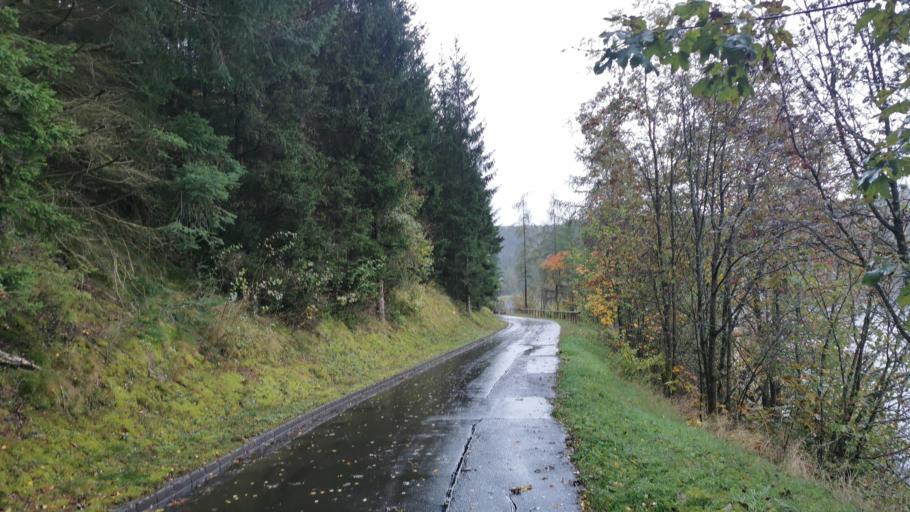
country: DE
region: Bavaria
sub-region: Upper Franconia
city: Steinwiesen
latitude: 50.3256
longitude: 11.4893
